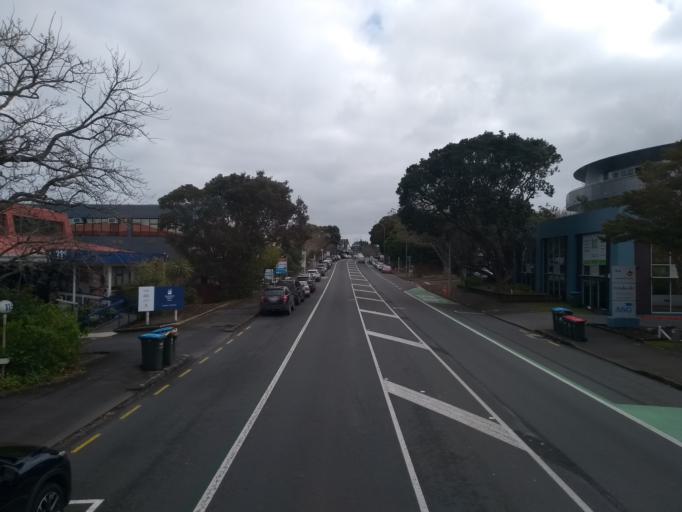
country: NZ
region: Auckland
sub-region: Auckland
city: Auckland
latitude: -36.8847
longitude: 174.7868
